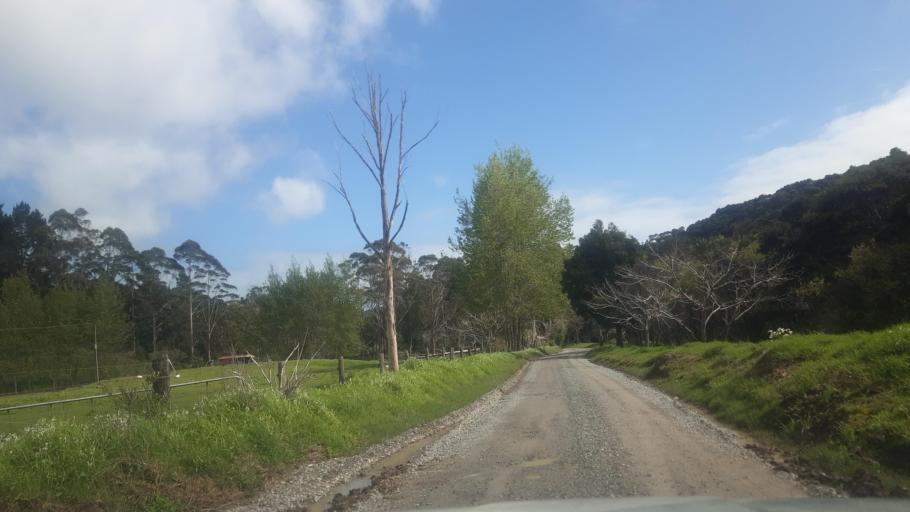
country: NZ
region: Northland
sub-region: Far North District
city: Taipa
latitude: -35.1141
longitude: 173.4310
